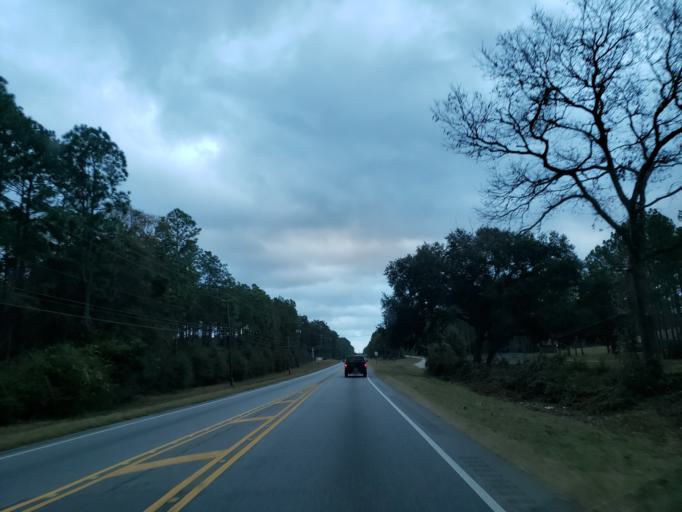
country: US
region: Alabama
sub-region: Mobile County
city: Chickasaw
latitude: 30.7886
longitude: -88.2914
